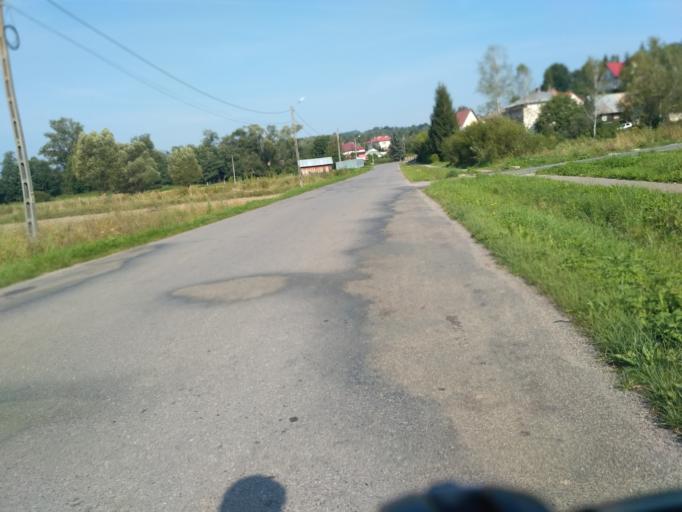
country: PL
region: Subcarpathian Voivodeship
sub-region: Powiat brzozowski
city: Blizne
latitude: 49.7853
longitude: 21.9886
